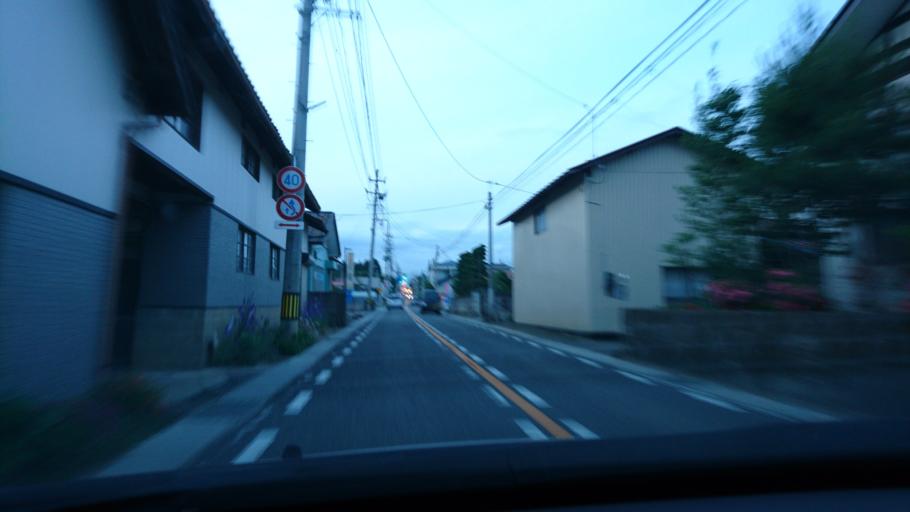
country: JP
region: Iwate
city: Ichinoseki
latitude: 38.8126
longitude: 140.9847
